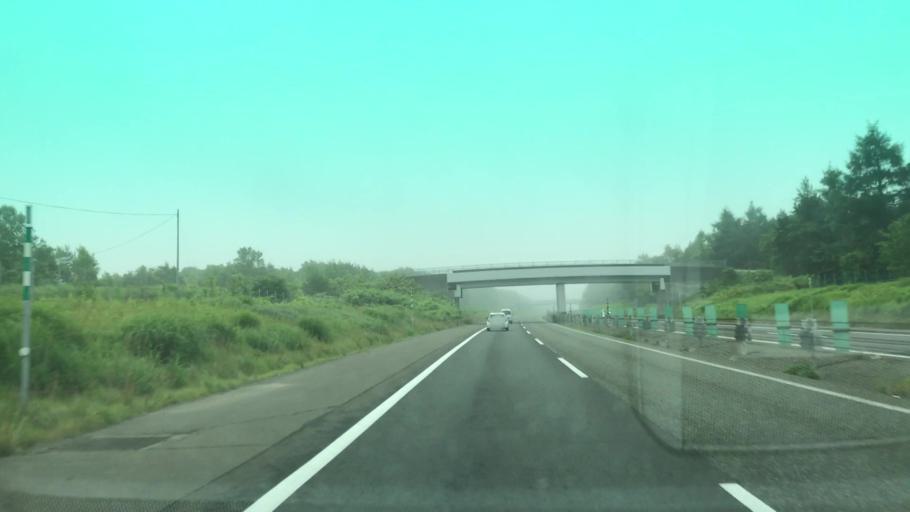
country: JP
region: Hokkaido
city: Chitose
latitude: 42.8276
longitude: 141.6141
